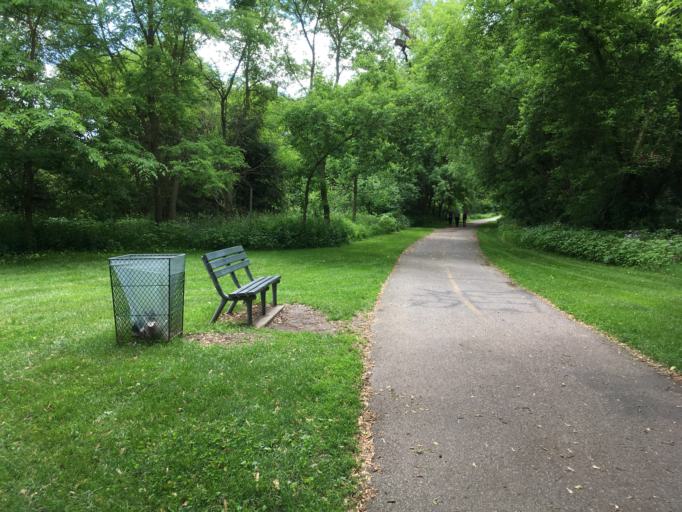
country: CA
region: Ontario
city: Oshawa
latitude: 43.8834
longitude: -78.8603
